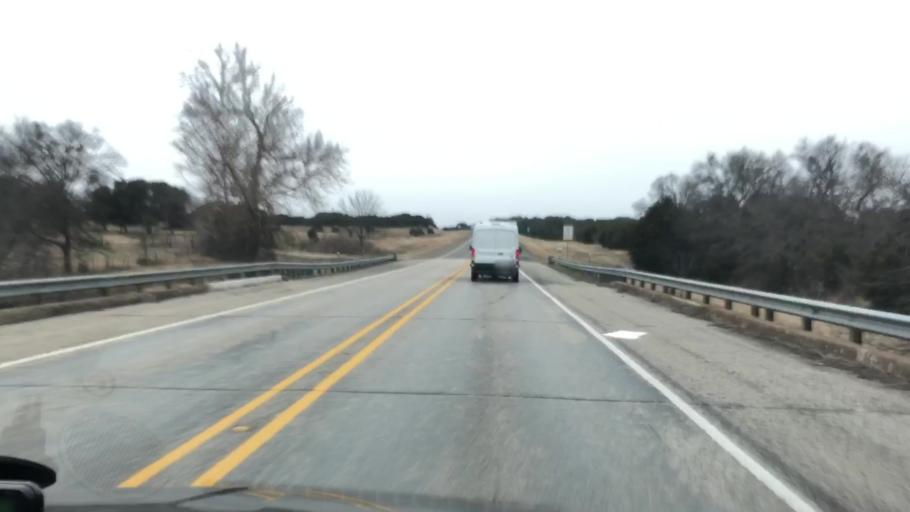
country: US
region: Texas
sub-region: Lampasas County
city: Lampasas
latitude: 31.1643
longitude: -98.1762
